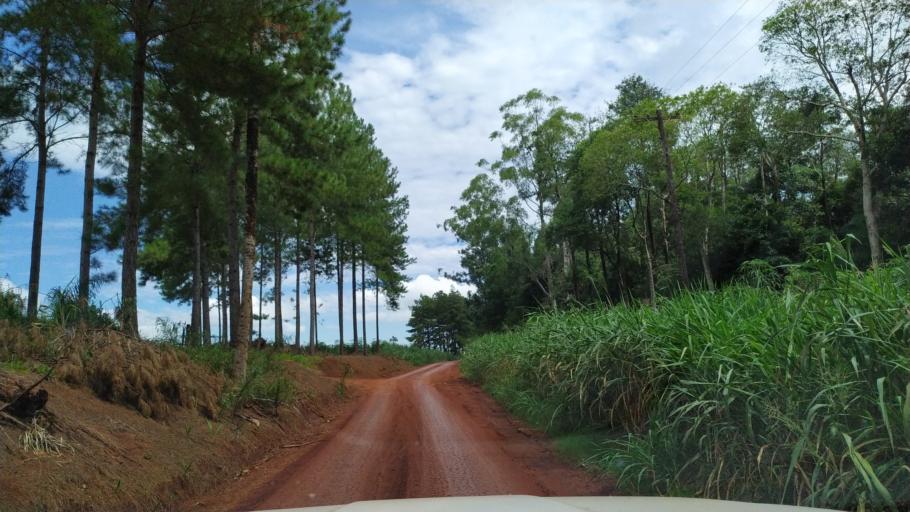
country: AR
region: Misiones
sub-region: Departamento de Eldorado
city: Eldorado
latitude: -26.5271
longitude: -54.5979
